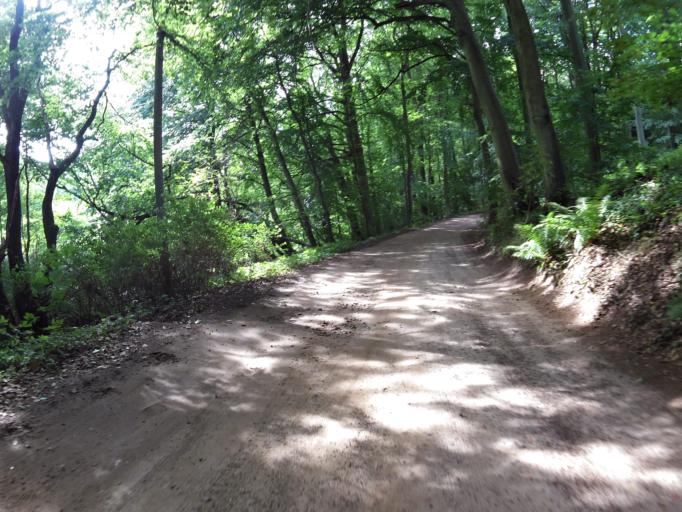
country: DE
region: Mecklenburg-Vorpommern
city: Seebad Bansin
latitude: 53.9627
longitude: 14.1083
